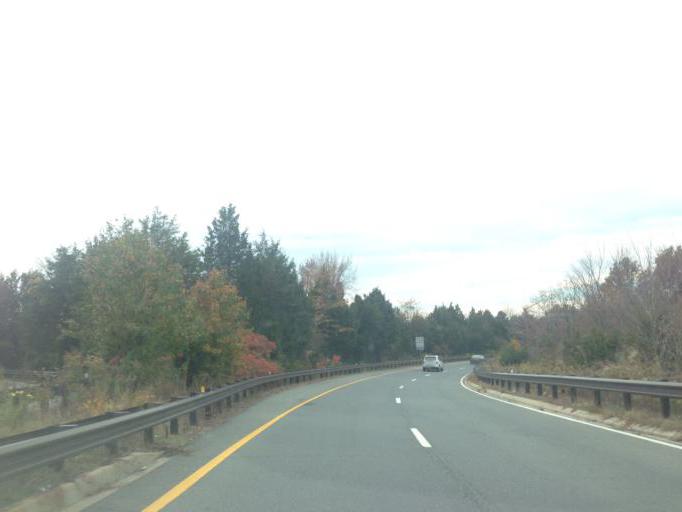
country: US
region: Maryland
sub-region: Montgomery County
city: Germantown
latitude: 39.1869
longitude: -77.2548
